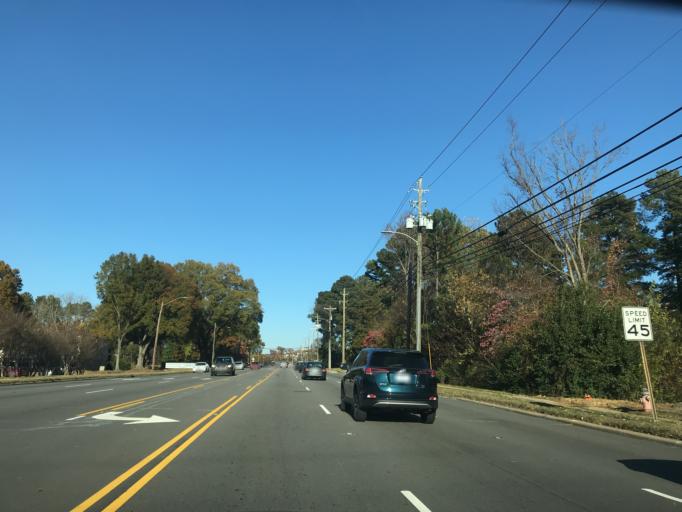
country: US
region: North Carolina
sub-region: Wake County
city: Raleigh
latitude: 35.8327
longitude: -78.6173
